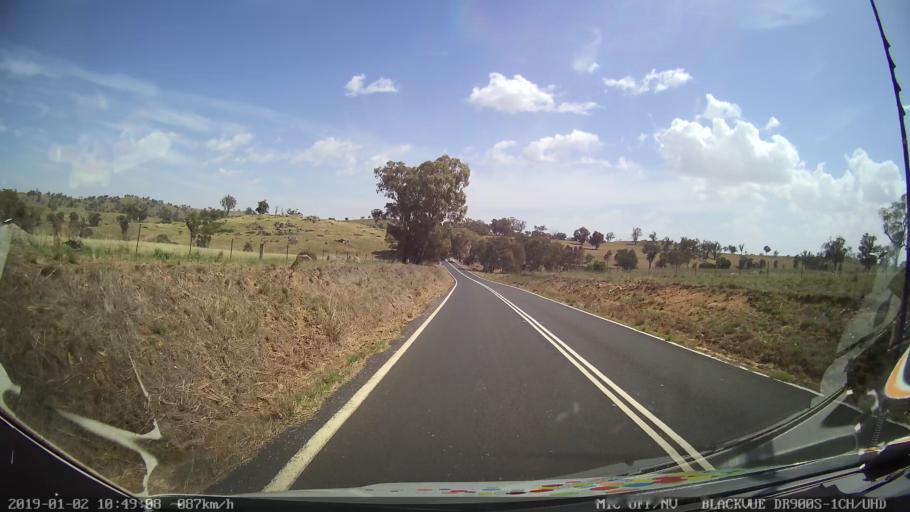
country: AU
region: New South Wales
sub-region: Cootamundra
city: Cootamundra
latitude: -34.7285
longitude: 148.2776
